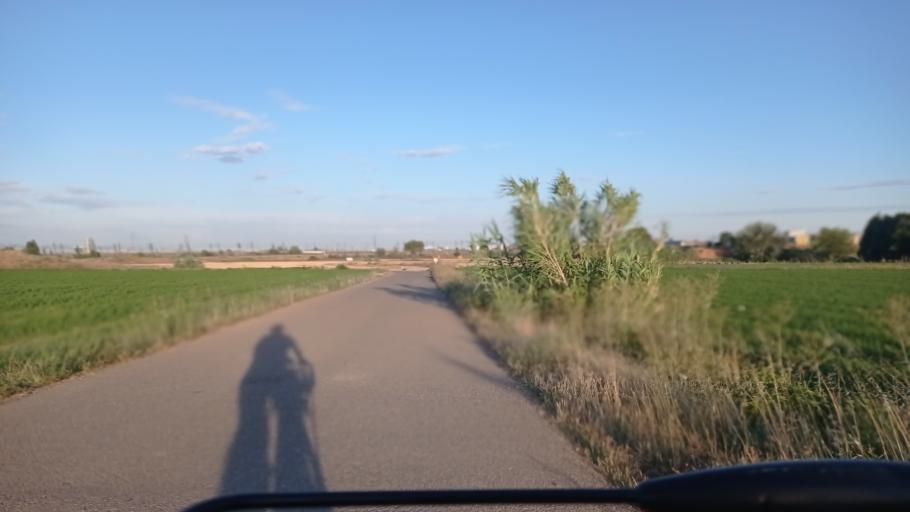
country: ES
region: Aragon
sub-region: Provincia de Zaragoza
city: Oliver-Valdefierro, Oliver, Valdefierro
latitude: 41.6745
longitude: -0.9429
